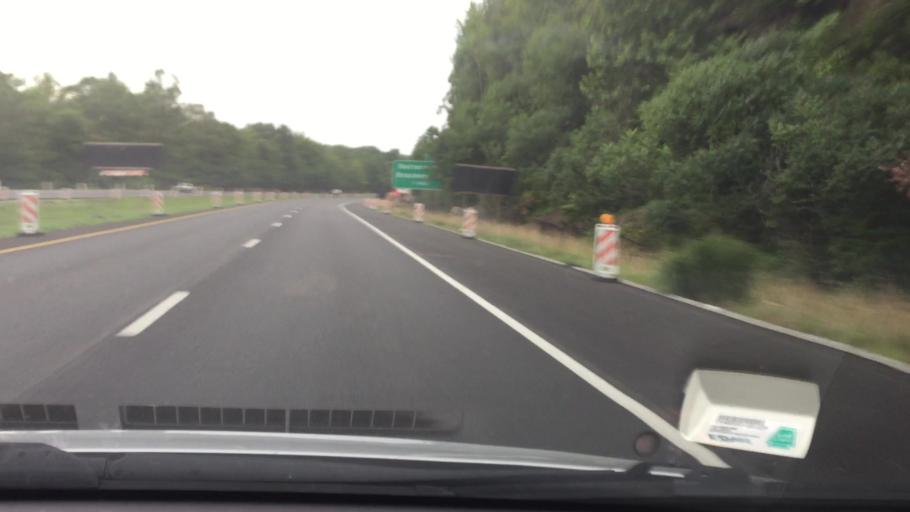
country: US
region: Pennsylvania
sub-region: Allegheny County
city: Brackenridge
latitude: 40.6470
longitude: -79.7214
